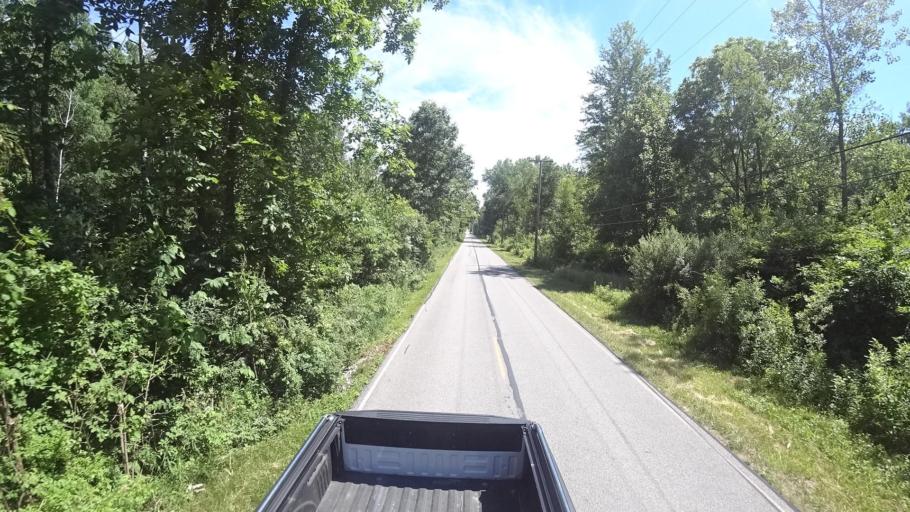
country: US
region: Indiana
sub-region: Porter County
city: Porter
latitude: 41.6470
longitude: -87.0674
